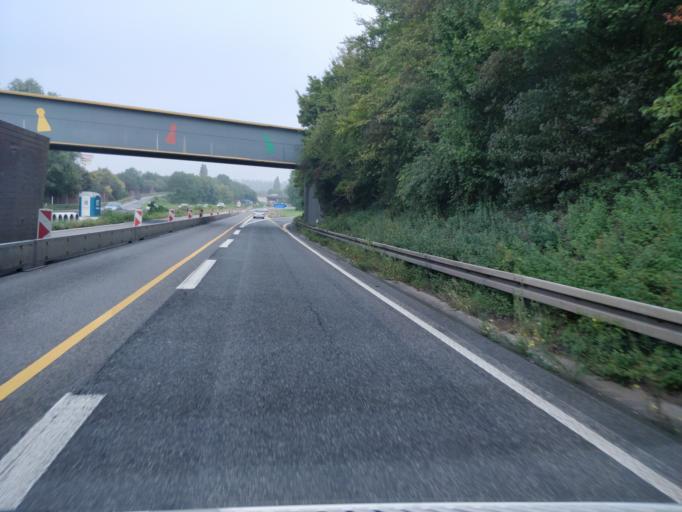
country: DE
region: North Rhine-Westphalia
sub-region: Regierungsbezirk Dusseldorf
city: Dinslaken
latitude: 51.5243
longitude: 6.7594
